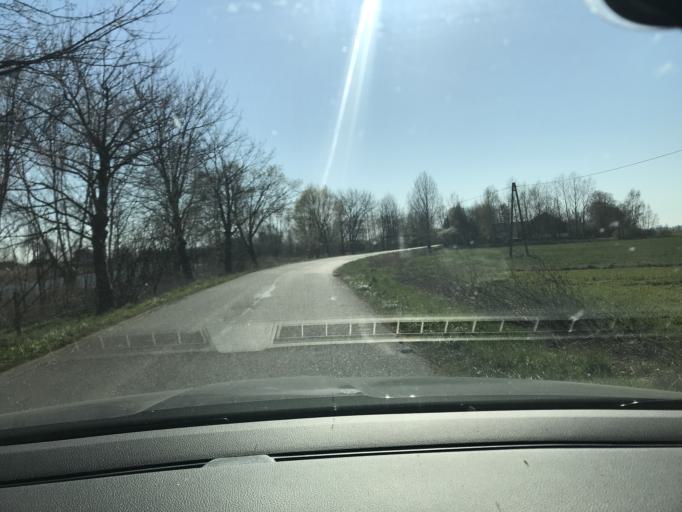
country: PL
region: Pomeranian Voivodeship
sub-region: Powiat nowodworski
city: Sztutowo
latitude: 54.2995
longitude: 19.1466
